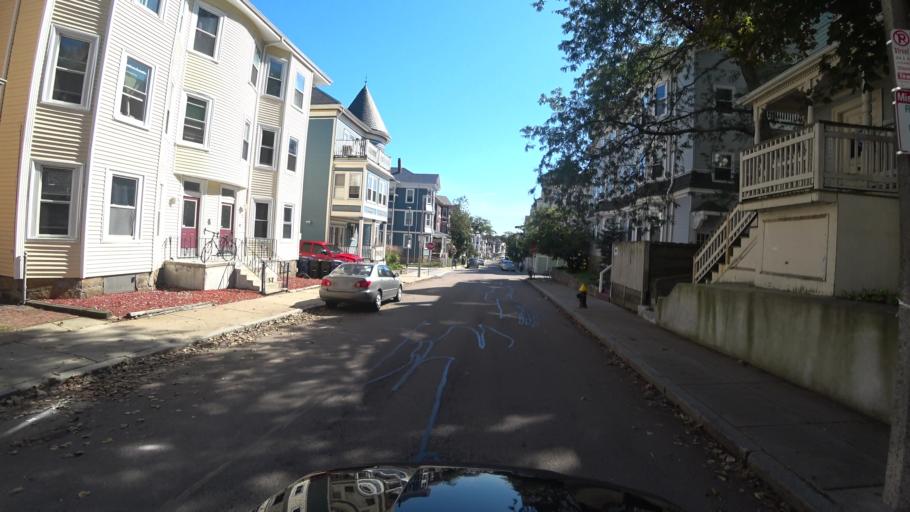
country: US
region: Massachusetts
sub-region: Norfolk County
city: Brookline
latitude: 42.3306
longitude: -71.1035
